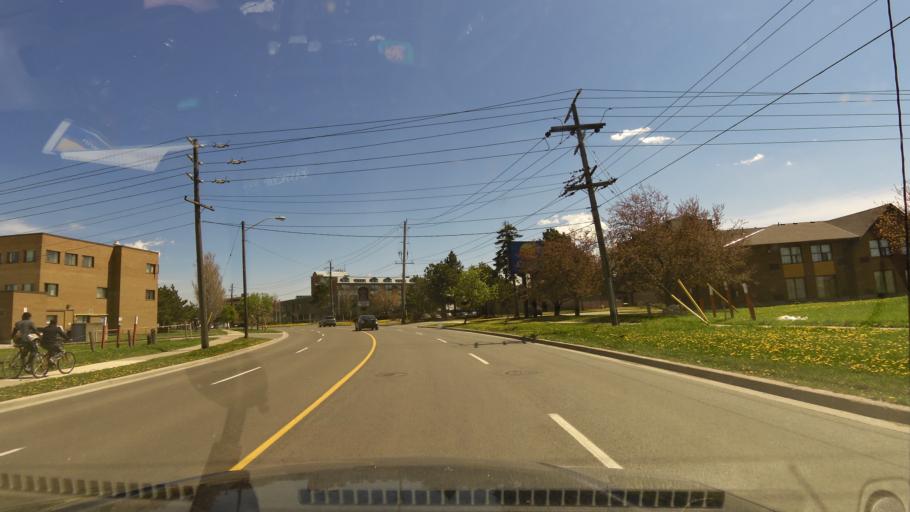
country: CA
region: Ontario
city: Concord
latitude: 43.7580
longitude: -79.5287
